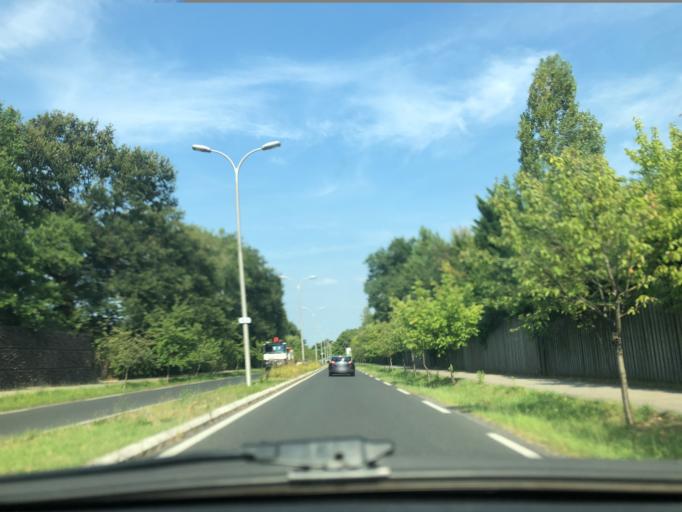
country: FR
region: Aquitaine
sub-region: Departement de la Gironde
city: Pessac
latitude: 44.8195
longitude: -0.6543
